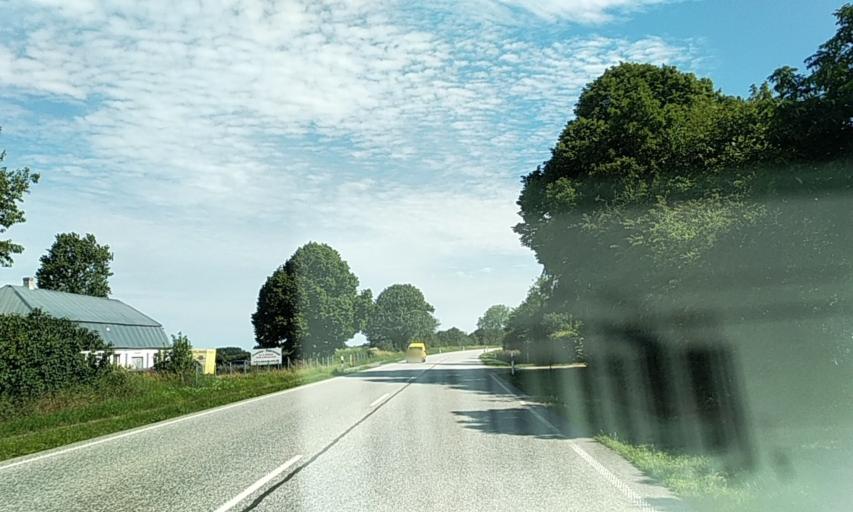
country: DE
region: Schleswig-Holstein
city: Jagel
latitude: 54.4380
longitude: 9.5336
